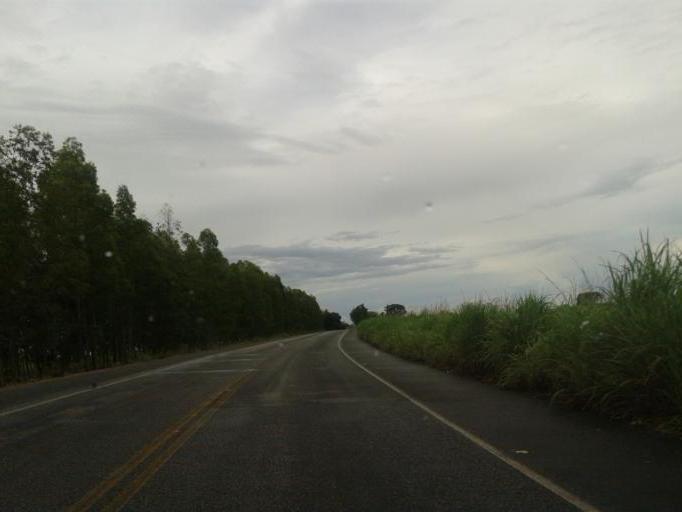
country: BR
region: Goias
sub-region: Mozarlandia
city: Mozarlandia
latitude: -14.8799
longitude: -50.5533
